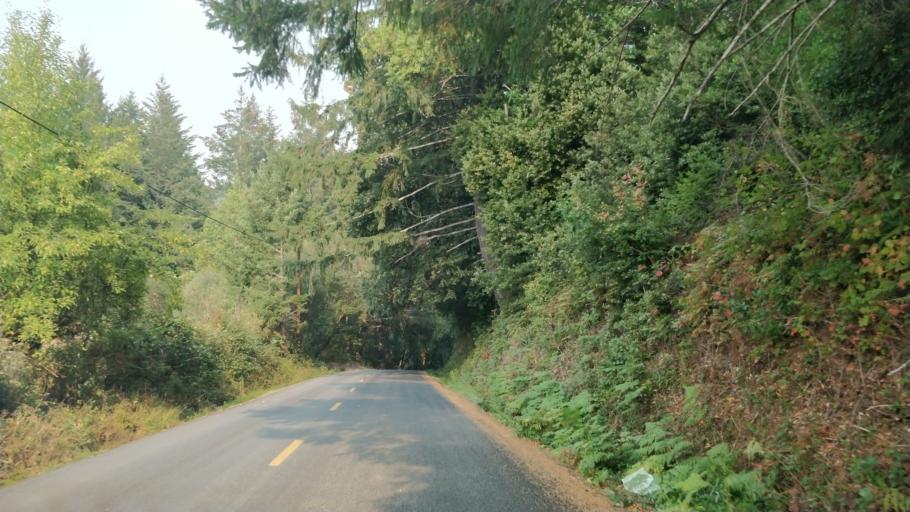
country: US
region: California
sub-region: Humboldt County
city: Rio Dell
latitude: 40.2699
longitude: -124.2078
